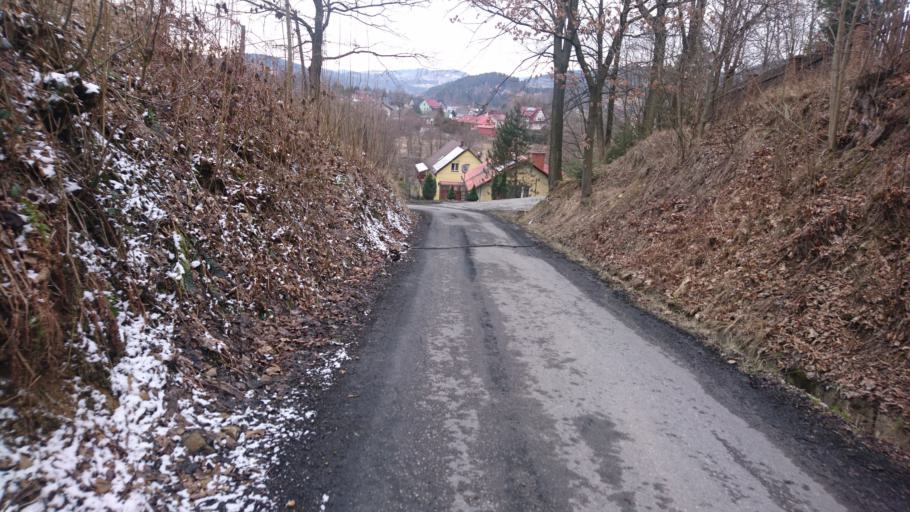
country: PL
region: Lesser Poland Voivodeship
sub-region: Powiat suski
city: Stryszawa
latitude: 49.7313
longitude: 19.5310
